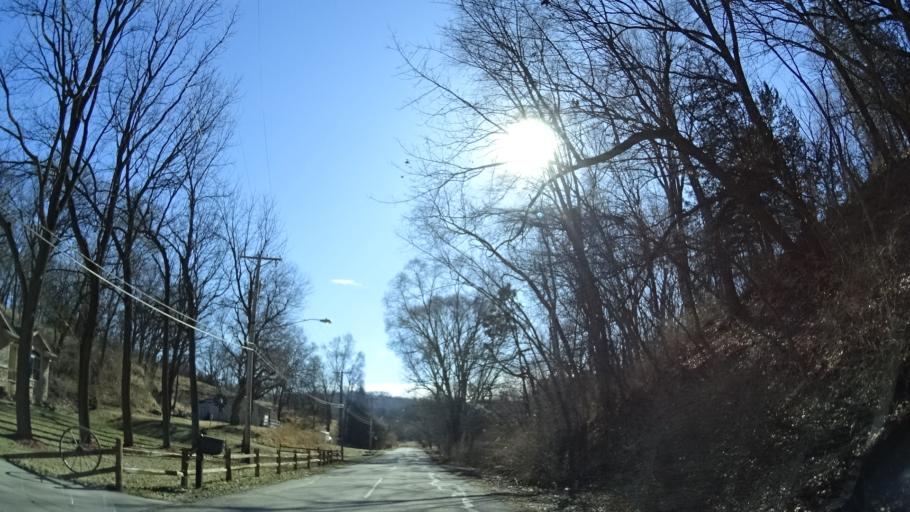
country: US
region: Nebraska
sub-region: Sarpy County
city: Bellevue
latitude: 41.1571
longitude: -95.8950
